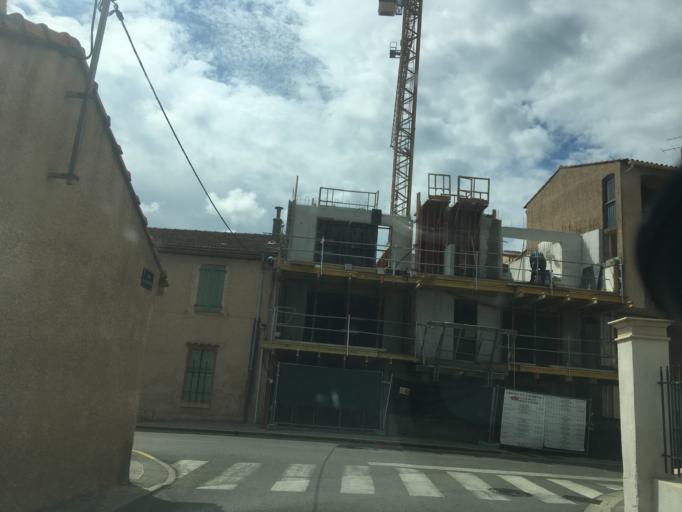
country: FR
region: Provence-Alpes-Cote d'Azur
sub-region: Departement du Var
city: La Londe-les-Maures
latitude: 43.1395
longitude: 6.2345
